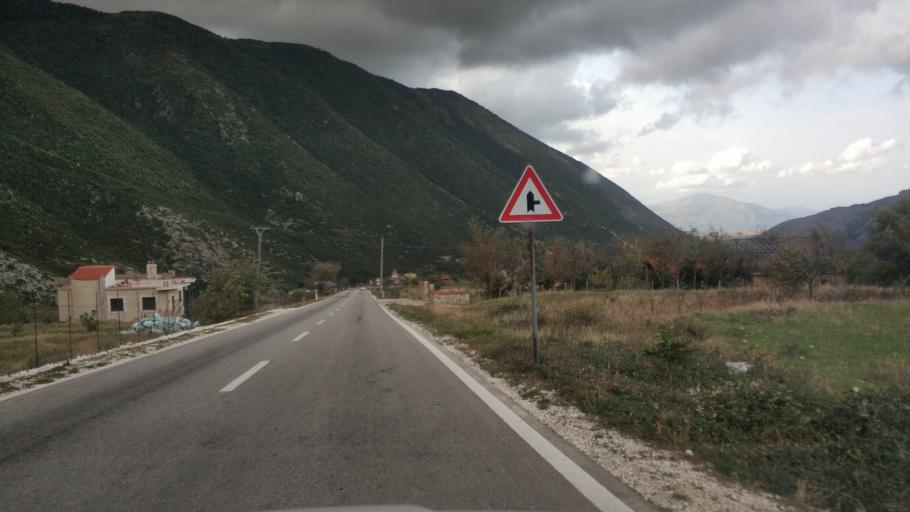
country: AL
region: Vlore
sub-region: Rrethi i Vlores
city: Brataj
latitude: 40.2316
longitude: 19.5662
